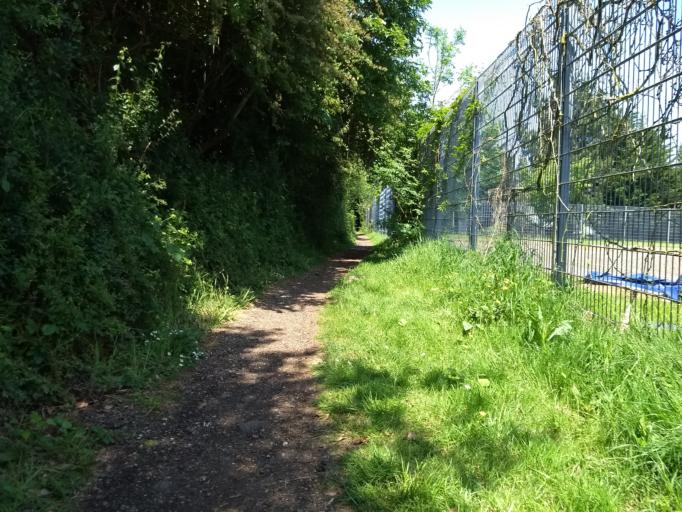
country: GB
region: England
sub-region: Isle of Wight
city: Northwood
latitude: 50.7503
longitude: -1.3086
